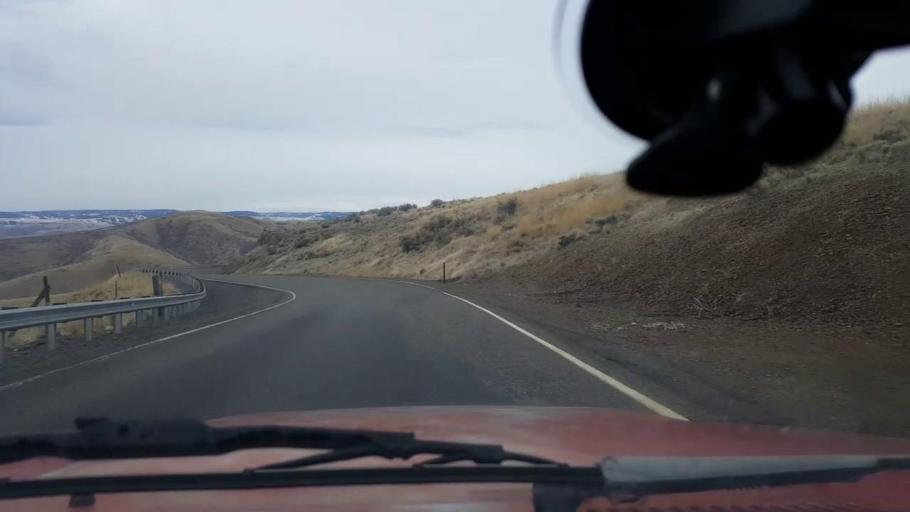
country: US
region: Washington
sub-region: Asotin County
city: Clarkston Heights-Vineland
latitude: 46.3354
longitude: -117.2804
